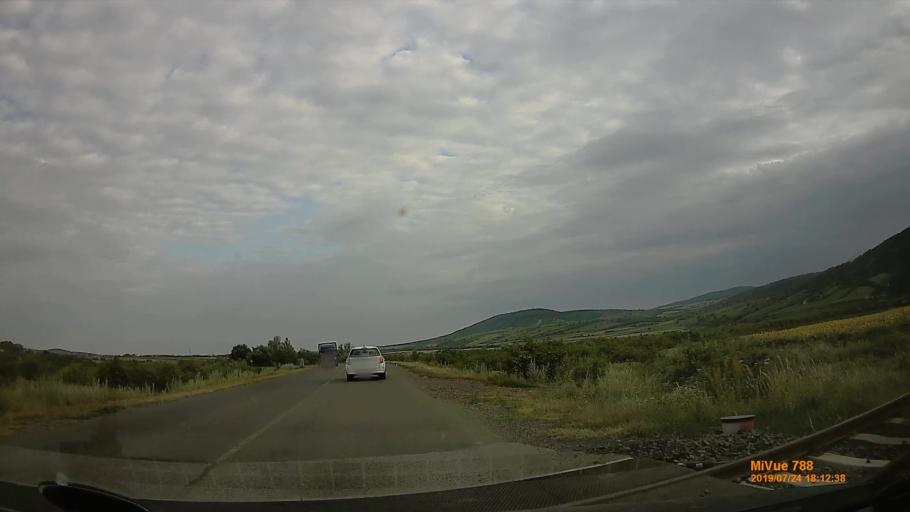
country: HU
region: Borsod-Abauj-Zemplen
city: Tallya
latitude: 48.2362
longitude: 21.2128
